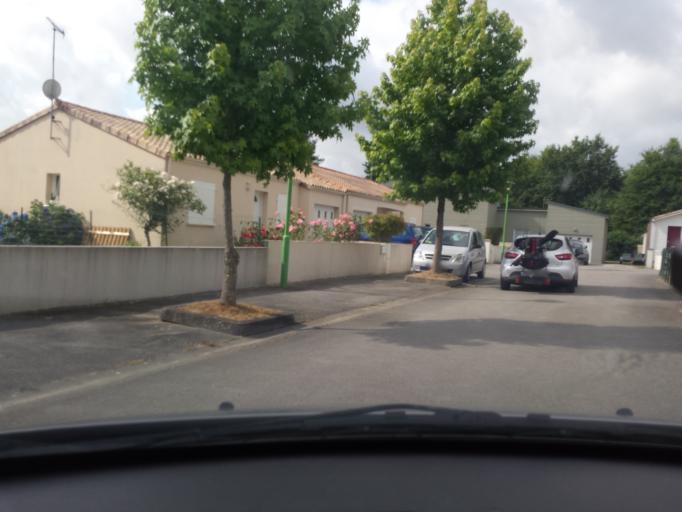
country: FR
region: Pays de la Loire
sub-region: Departement de la Vendee
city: Dompierre-sur-Yon
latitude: 46.7455
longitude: -1.3832
